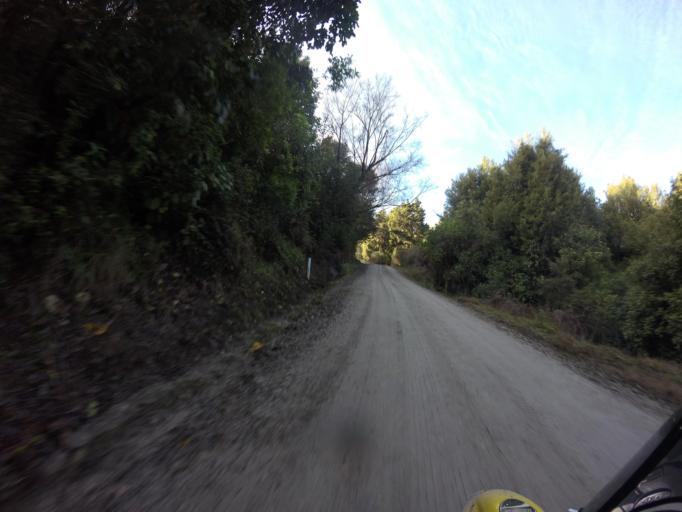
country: NZ
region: Hawke's Bay
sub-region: Wairoa District
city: Wairoa
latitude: -38.7475
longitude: 177.5228
